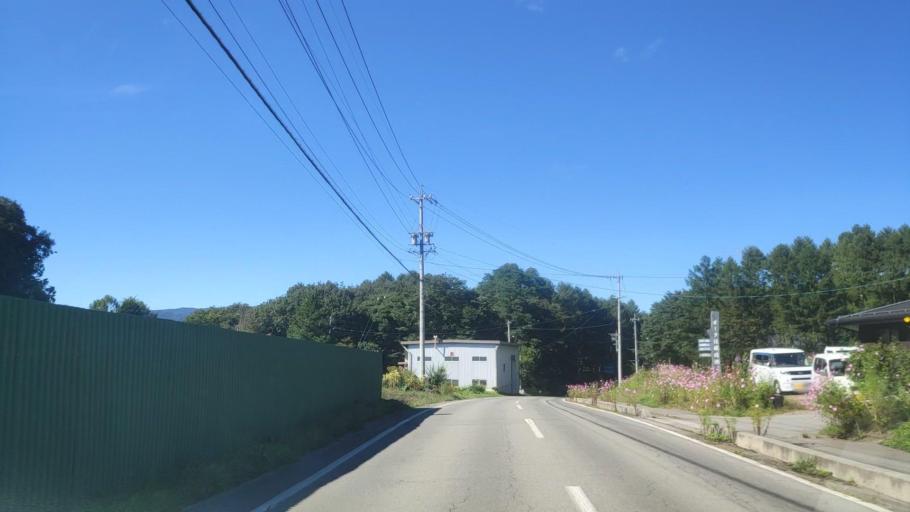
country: JP
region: Nagano
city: Chino
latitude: 36.0078
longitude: 138.2086
